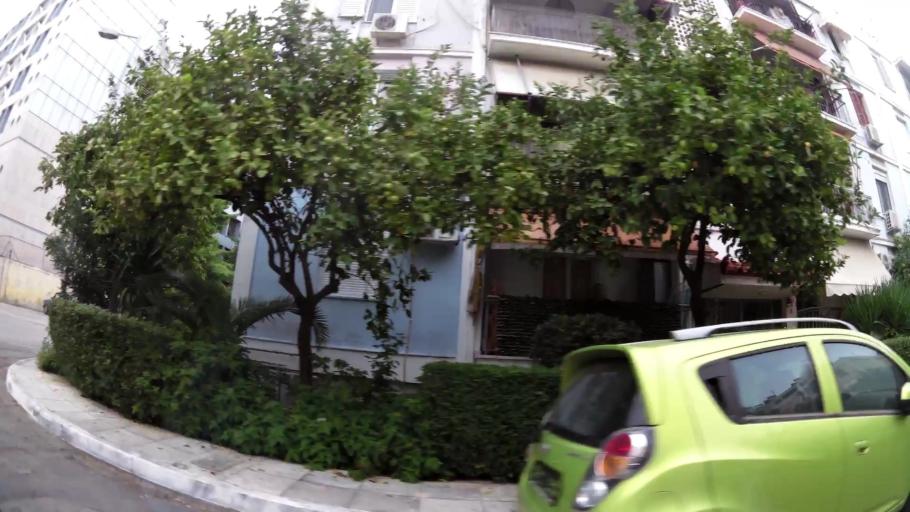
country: GR
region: Attica
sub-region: Nomos Piraios
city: Agios Ioannis Rentis
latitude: 37.9665
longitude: 23.6626
